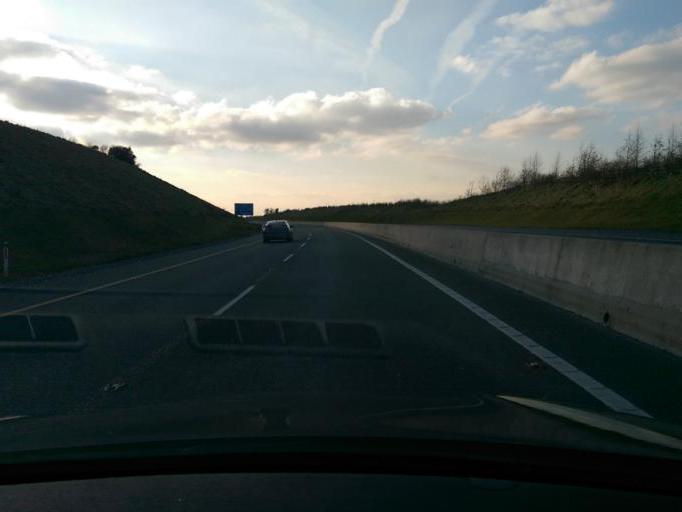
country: IE
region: Leinster
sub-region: Laois
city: Rathdowney
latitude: 52.9258
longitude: -7.5883
